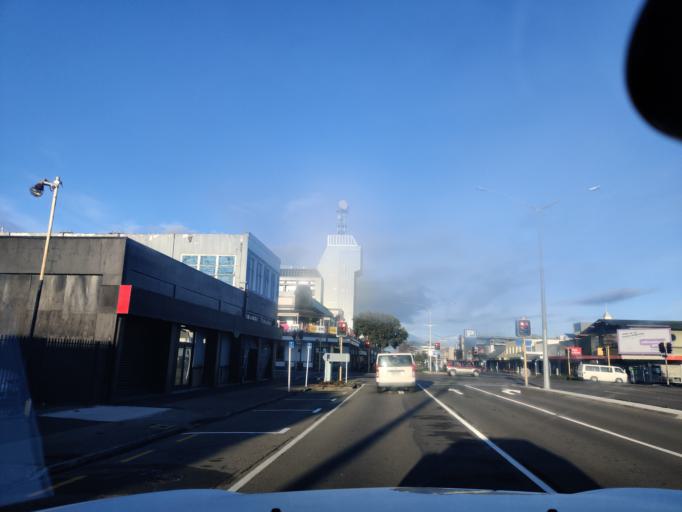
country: NZ
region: Manawatu-Wanganui
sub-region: Palmerston North City
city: Palmerston North
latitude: -40.3542
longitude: 175.6161
